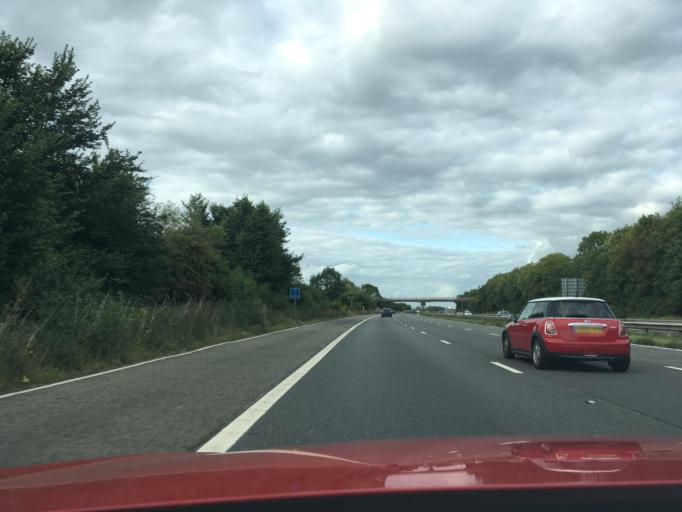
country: GB
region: England
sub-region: Gloucestershire
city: Stonehouse
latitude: 51.7758
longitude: -2.3100
